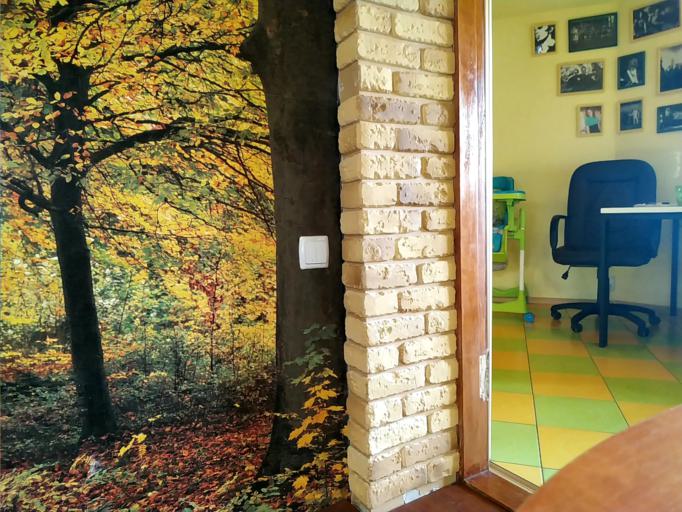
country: RU
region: Jaroslavl
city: Krasnyy Profintern
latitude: 58.0125
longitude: 40.4781
